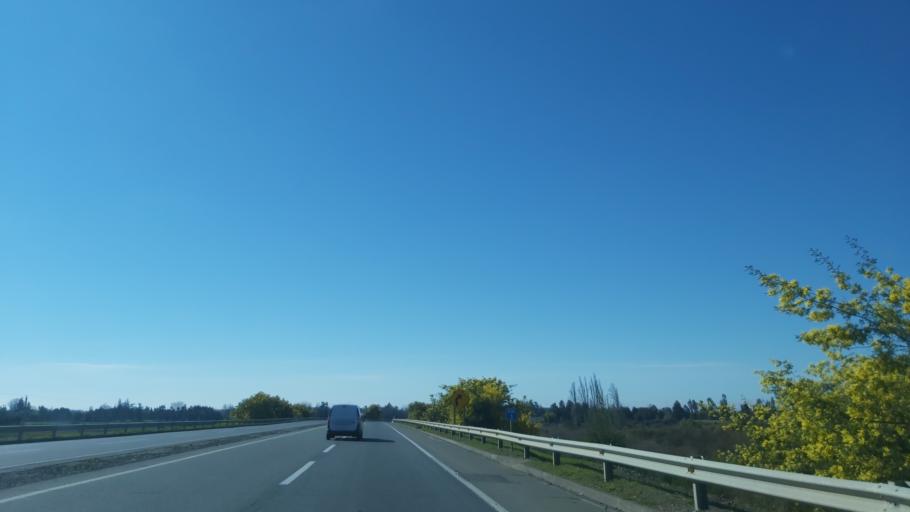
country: CL
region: Biobio
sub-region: Provincia de Nuble
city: Bulnes
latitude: -36.6550
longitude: -72.2416
